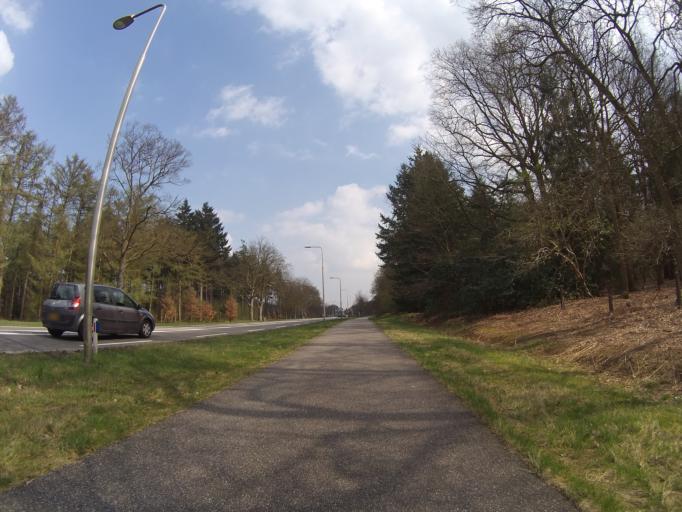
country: NL
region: North Holland
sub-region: Gemeente Laren
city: Laren
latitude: 52.2037
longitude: 5.2306
